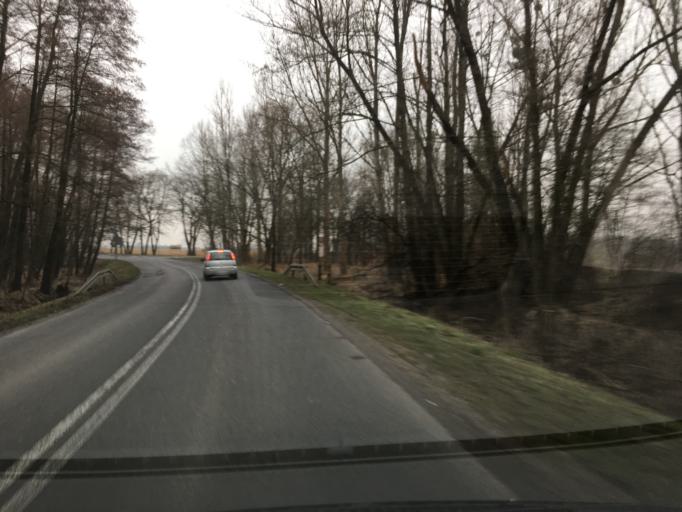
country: PL
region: Opole Voivodeship
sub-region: Powiat kedzierzynsko-kozielski
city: Bierawa
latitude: 50.2979
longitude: 18.2329
